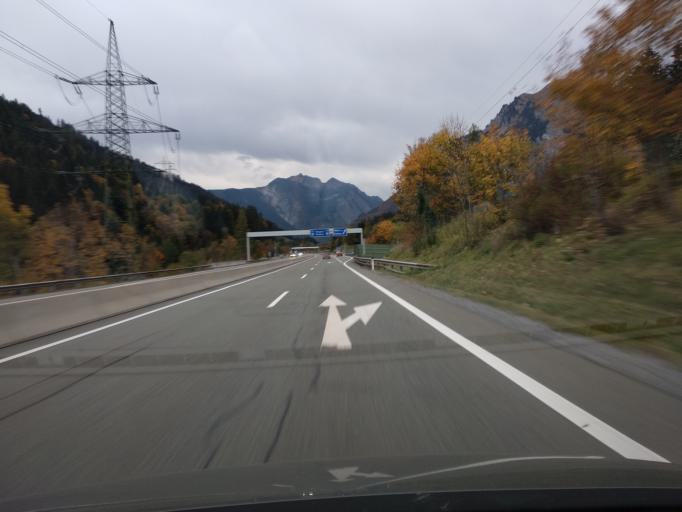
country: AT
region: Vorarlberg
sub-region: Politischer Bezirk Bludenz
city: Klosterle
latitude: 47.1293
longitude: 10.0557
